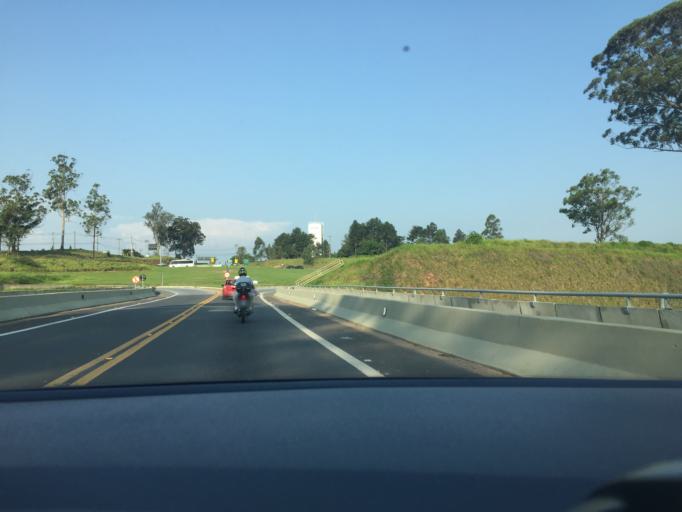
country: BR
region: Sao Paulo
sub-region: Valinhos
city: Valinhos
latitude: -23.0108
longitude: -47.0246
